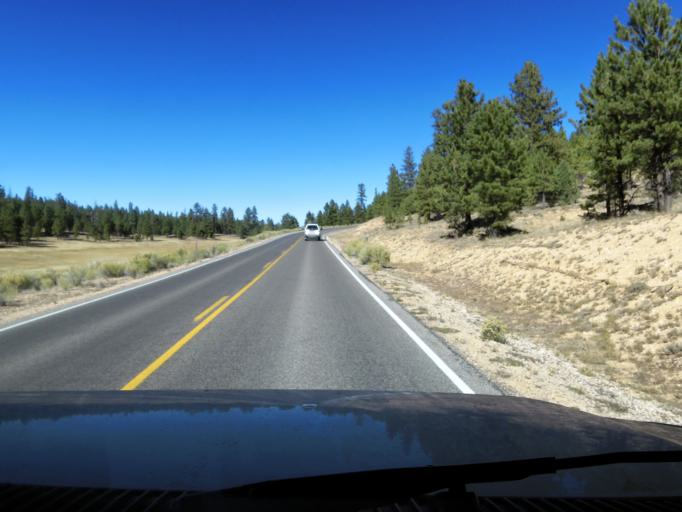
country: US
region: Utah
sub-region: Garfield County
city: Panguitch
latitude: 37.6007
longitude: -112.2080
